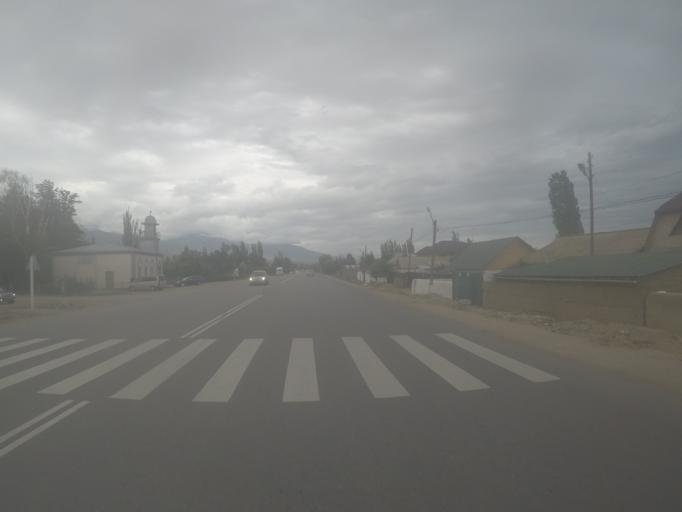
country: KG
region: Ysyk-Koel
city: Cholpon-Ata
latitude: 42.5866
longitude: 76.7433
